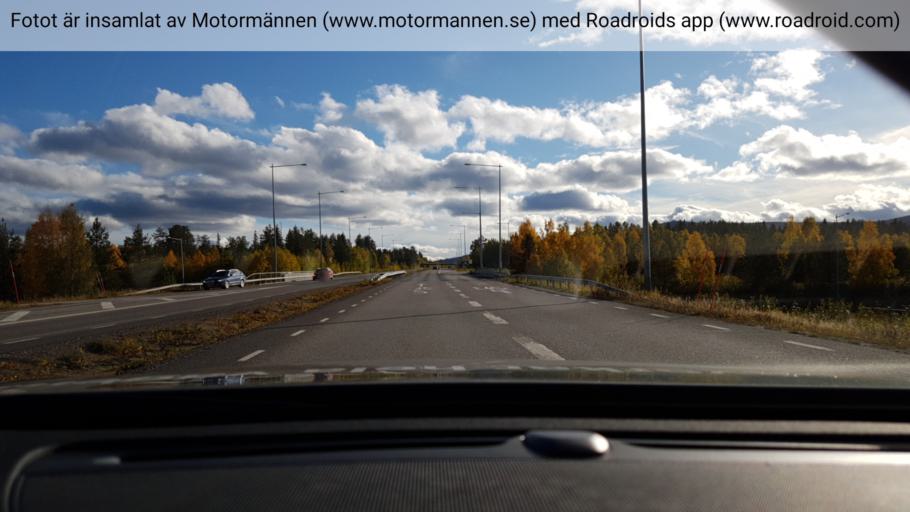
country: SE
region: Norrbotten
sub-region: Gallivare Kommun
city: Gaellivare
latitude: 67.1480
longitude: 20.6637
